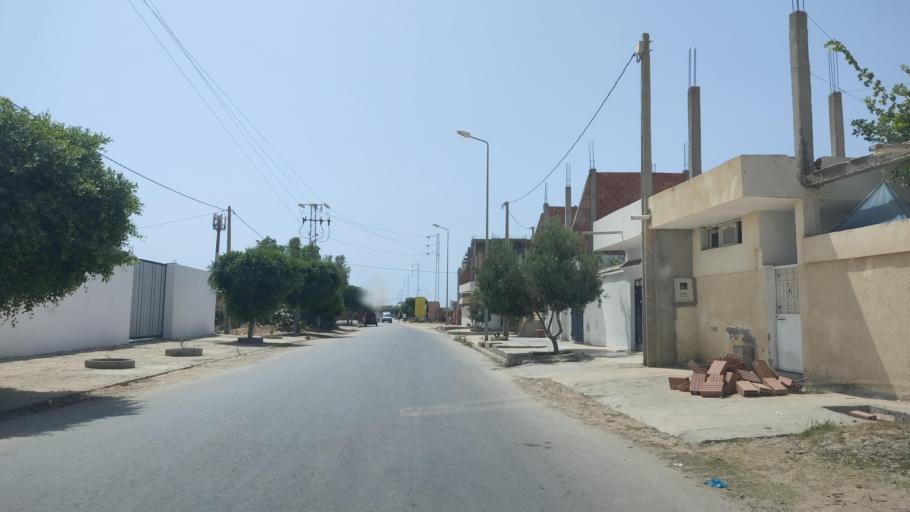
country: TN
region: Safaqis
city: Sfax
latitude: 34.6704
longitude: 10.7053
